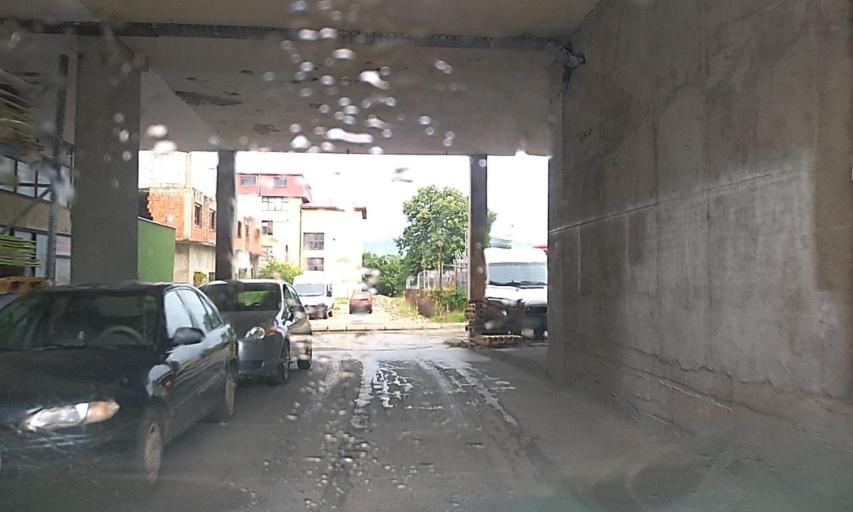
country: RS
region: Central Serbia
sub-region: Nisavski Okrug
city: Nis
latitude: 43.3046
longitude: 21.9524
